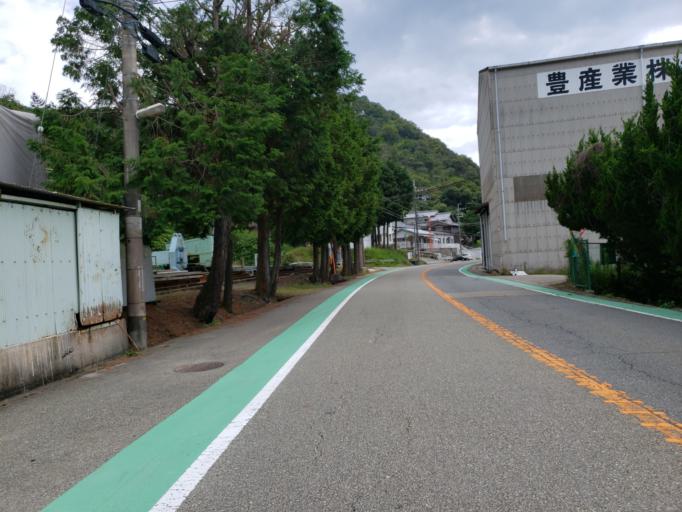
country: JP
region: Hyogo
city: Aioi
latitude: 34.7744
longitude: 134.4724
